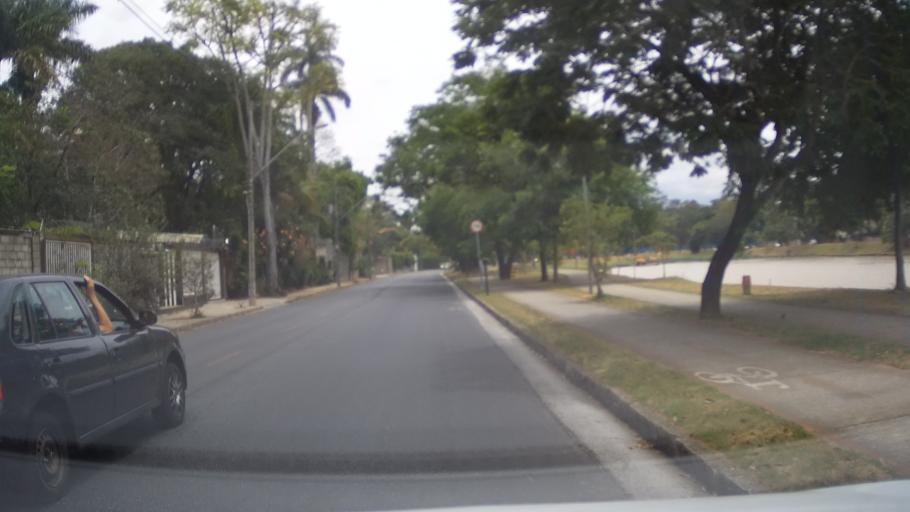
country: BR
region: Minas Gerais
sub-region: Belo Horizonte
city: Belo Horizonte
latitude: -19.8477
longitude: -43.9965
